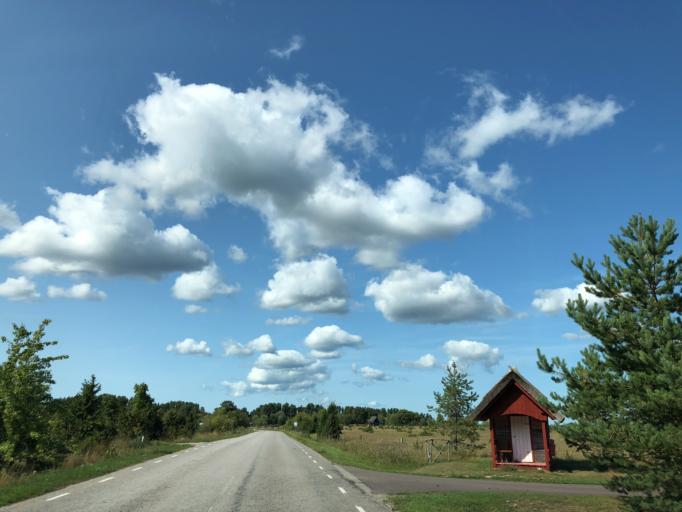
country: EE
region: Hiiumaa
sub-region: Kaerdla linn
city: Kardla
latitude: 58.7976
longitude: 22.7652
